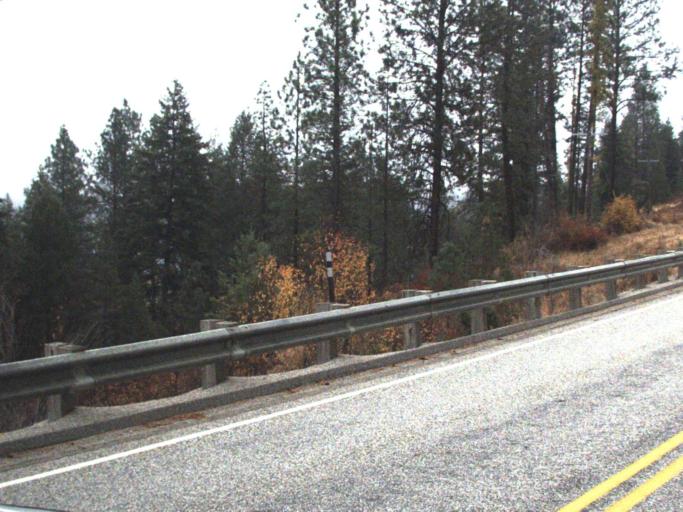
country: US
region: Washington
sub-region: Stevens County
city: Kettle Falls
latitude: 48.7466
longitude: -118.1347
